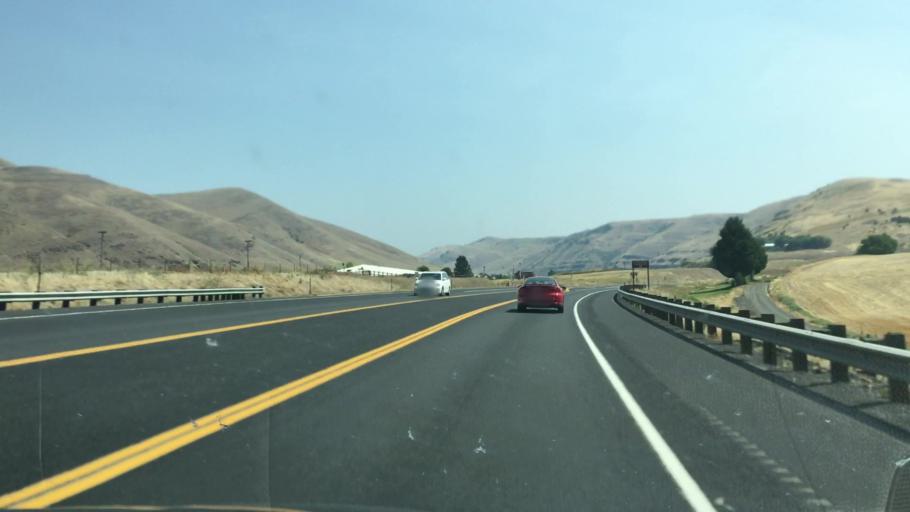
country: US
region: Idaho
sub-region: Nez Perce County
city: Lapwai
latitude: 46.4461
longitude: -116.8264
